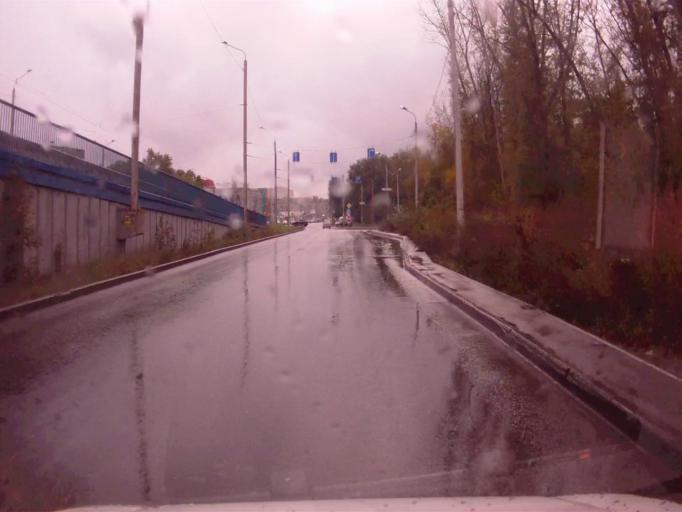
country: RU
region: Chelyabinsk
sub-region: Gorod Chelyabinsk
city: Chelyabinsk
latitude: 55.1953
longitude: 61.3879
